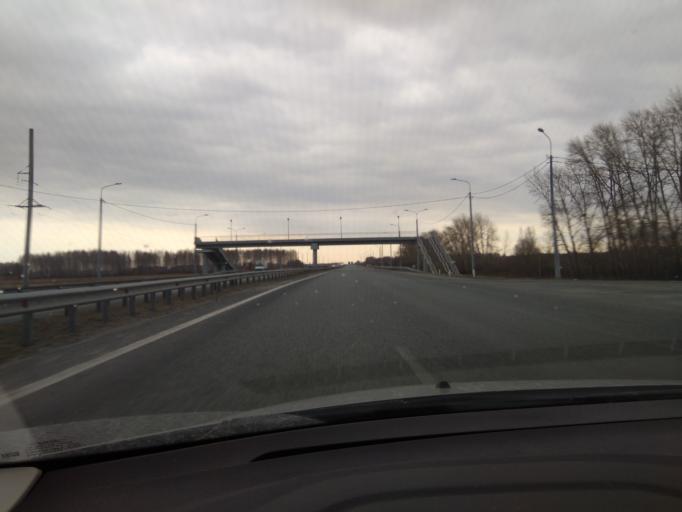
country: RU
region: Chelyabinsk
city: Kunashak
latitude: 55.7490
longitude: 61.2258
